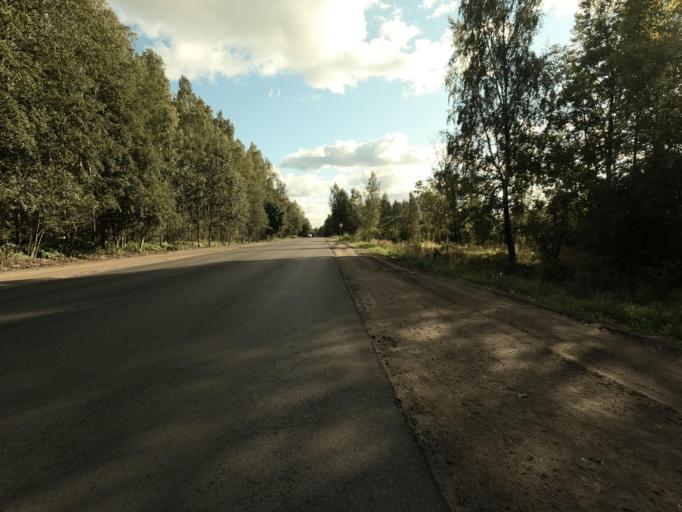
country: RU
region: Leningrad
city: Koltushi
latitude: 59.9292
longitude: 30.6642
